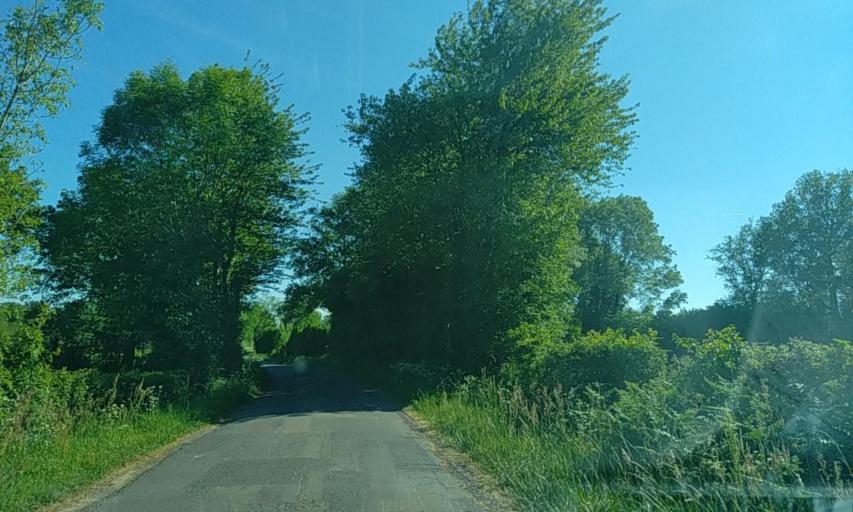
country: FR
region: Poitou-Charentes
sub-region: Departement des Deux-Sevres
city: Boisme
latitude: 46.7827
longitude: -0.4272
